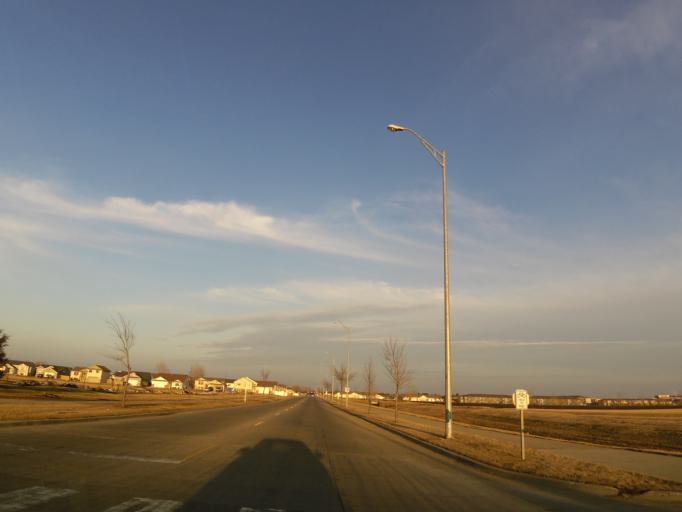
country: US
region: North Dakota
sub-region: Grand Forks County
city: Grand Forks
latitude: 47.8822
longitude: -97.0576
